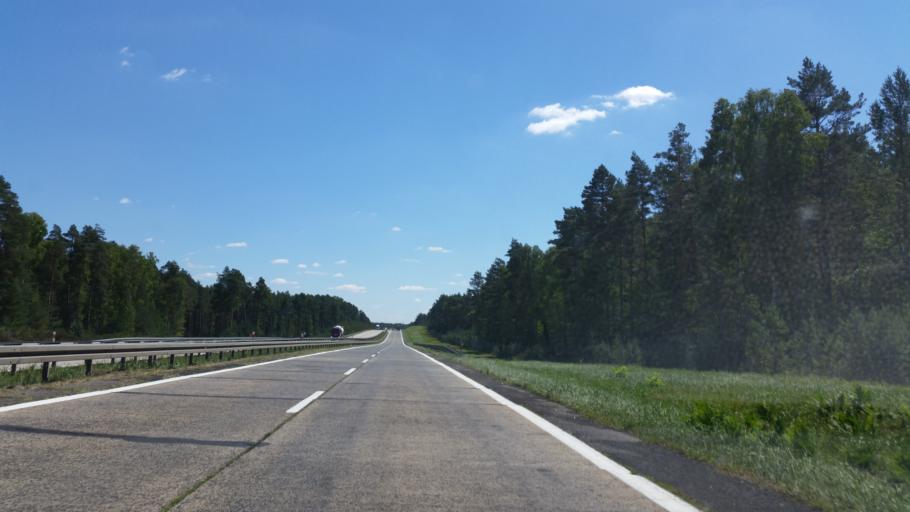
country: PL
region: Lubusz
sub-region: Powiat zaganski
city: Malomice
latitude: 51.4094
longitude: 15.5013
